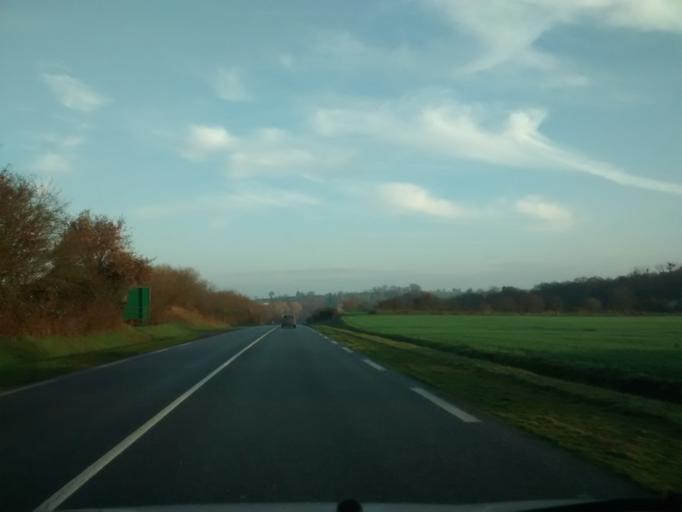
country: FR
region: Brittany
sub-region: Departement d'Ille-et-Vilaine
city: Sens-de-Bretagne
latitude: 48.3462
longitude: -1.5197
